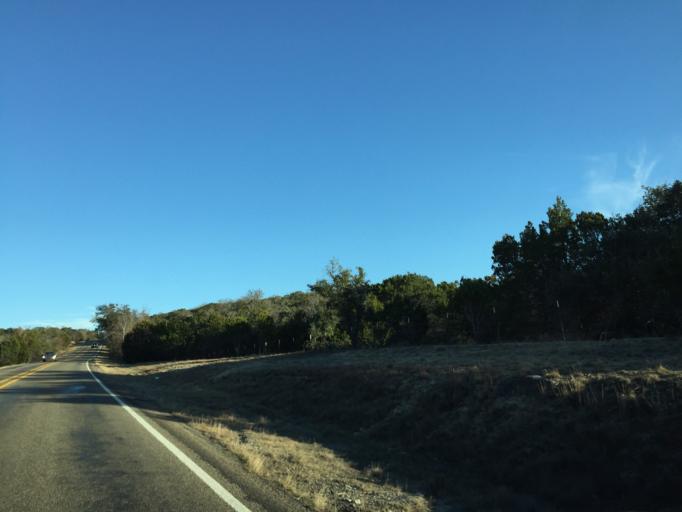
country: US
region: Texas
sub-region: Travis County
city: Lago Vista
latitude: 30.5240
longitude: -98.0848
